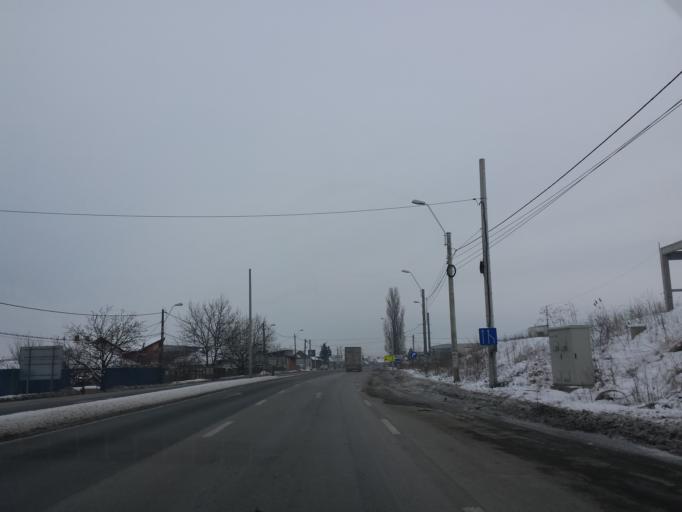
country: RO
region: Hunedoara
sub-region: Municipiul Deva
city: Cristur
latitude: 45.8582
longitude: 22.9417
